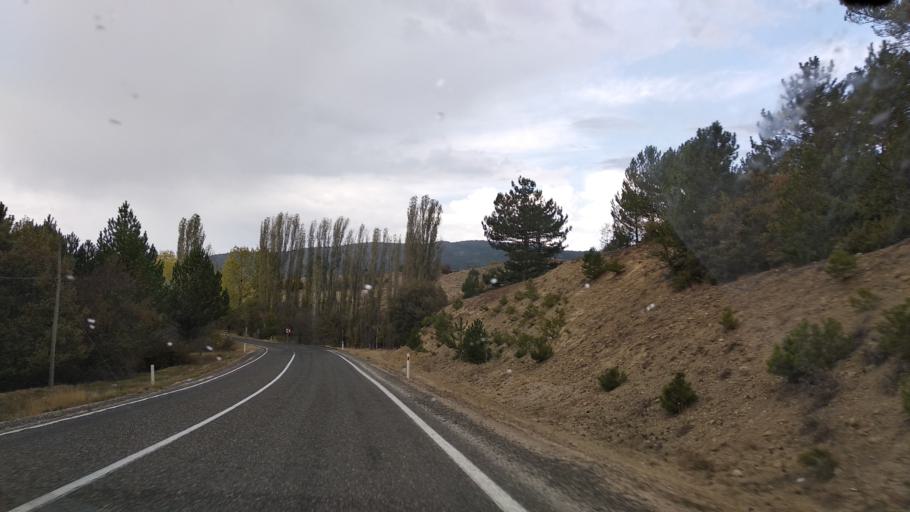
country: TR
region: Bolu
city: Seben
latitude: 40.3375
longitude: 31.4279
